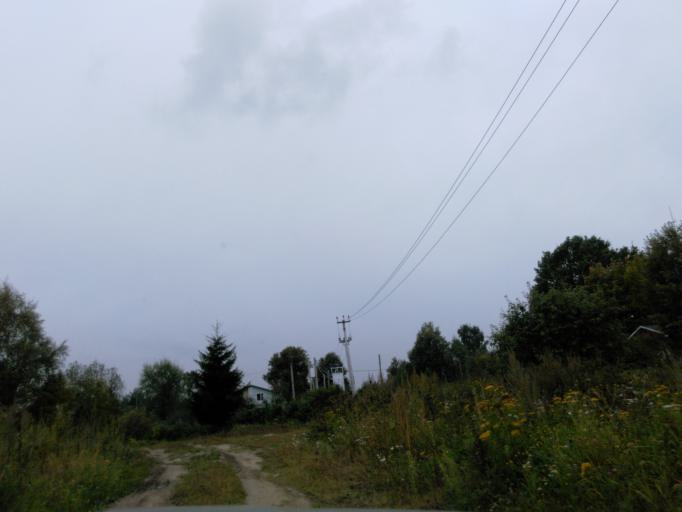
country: RU
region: Moskovskaya
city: Lozhki
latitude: 56.0605
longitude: 37.0982
